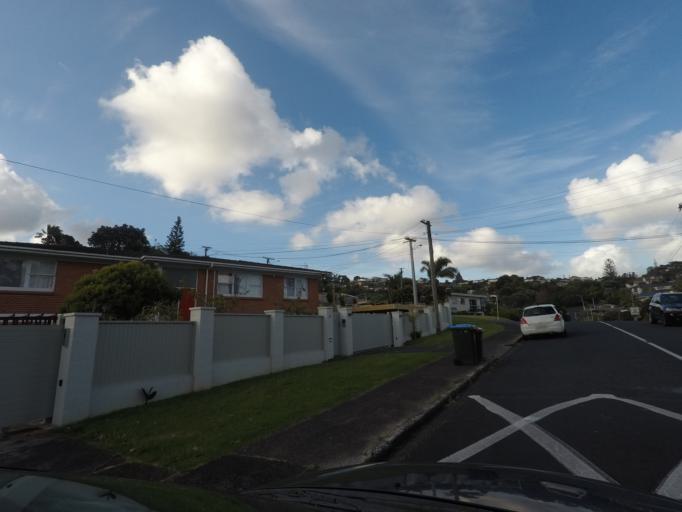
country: NZ
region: Auckland
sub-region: Auckland
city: Mangere
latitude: -36.9266
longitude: 174.7599
